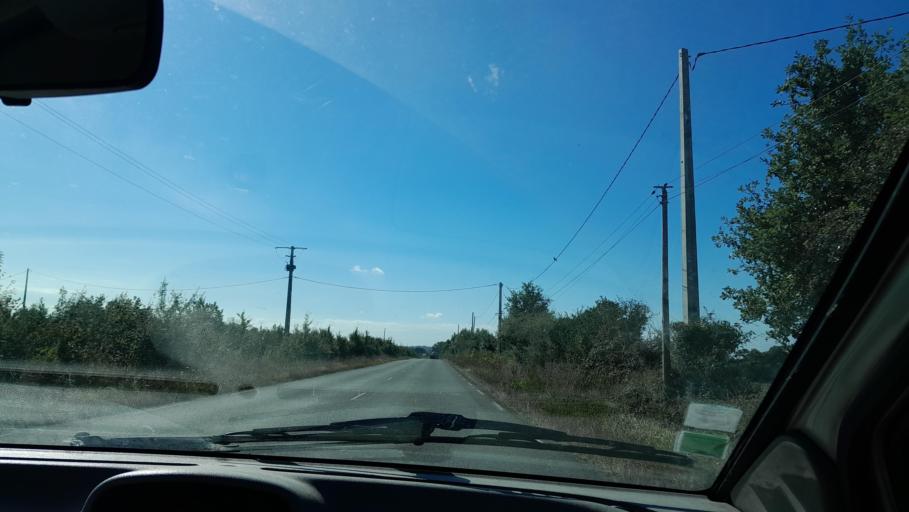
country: FR
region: Pays de la Loire
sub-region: Departement de la Mayenne
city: Ballots
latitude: 47.9232
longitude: -1.0696
